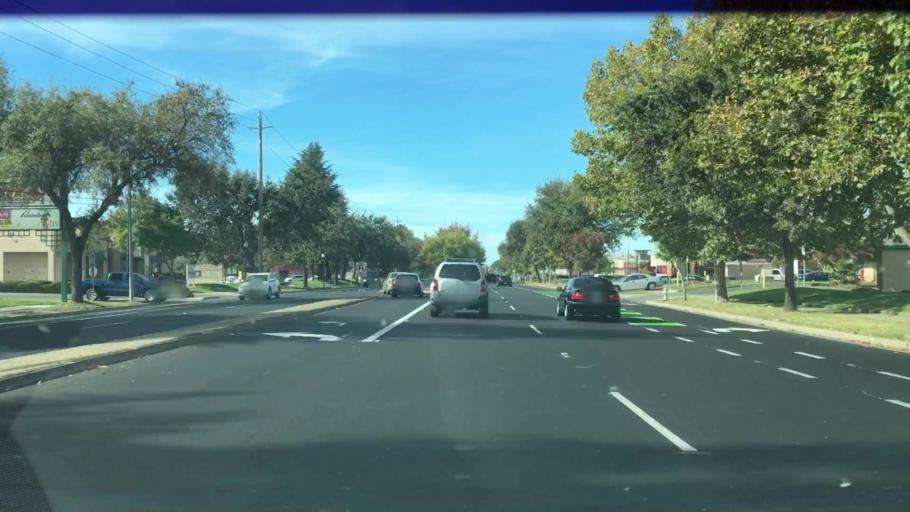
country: US
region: California
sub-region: Sacramento County
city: Florin
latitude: 38.4743
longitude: -121.4288
